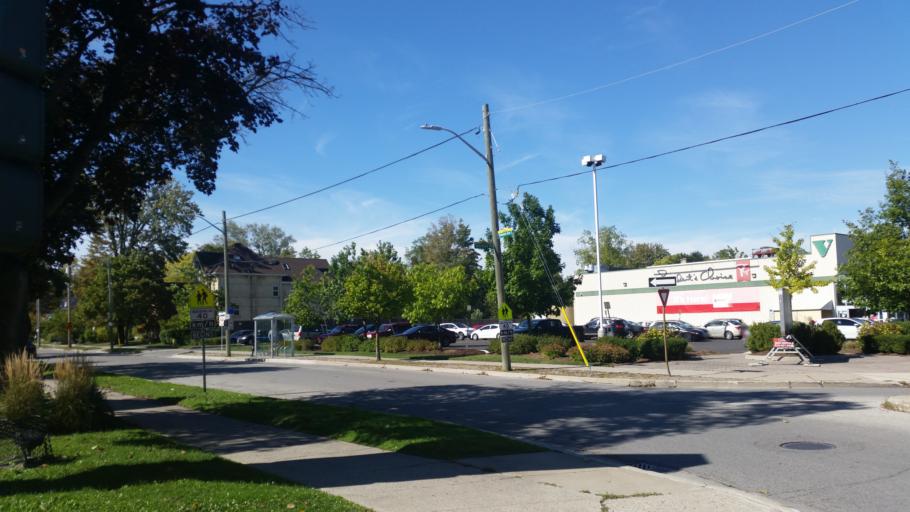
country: CA
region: Ontario
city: London
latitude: 42.9709
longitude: -81.2522
